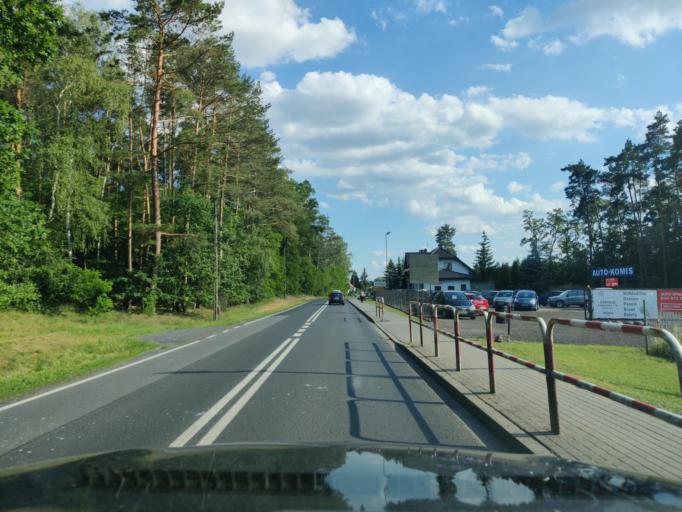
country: PL
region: Greater Poland Voivodeship
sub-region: Powiat wolsztynski
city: Wolsztyn
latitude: 52.1360
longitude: 16.1249
